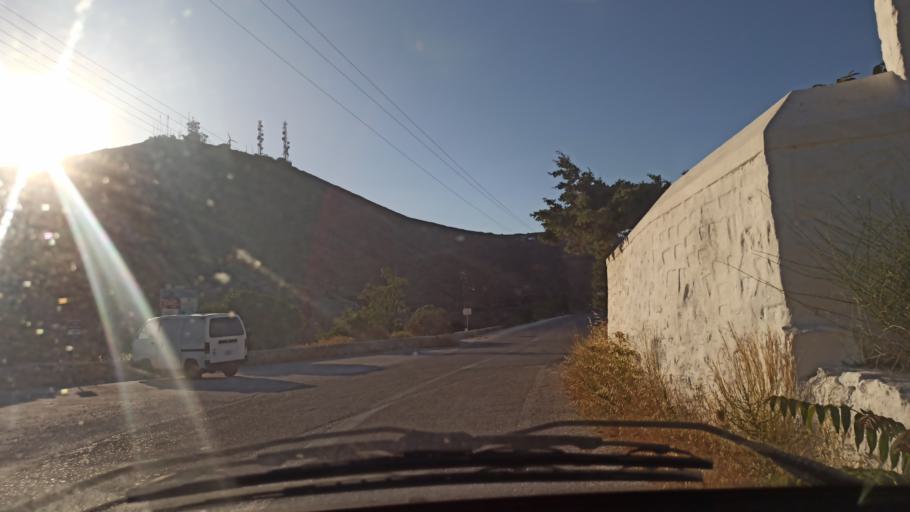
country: GR
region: South Aegean
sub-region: Nomos Kykladon
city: Ano Syros
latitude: 37.4532
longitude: 24.9341
